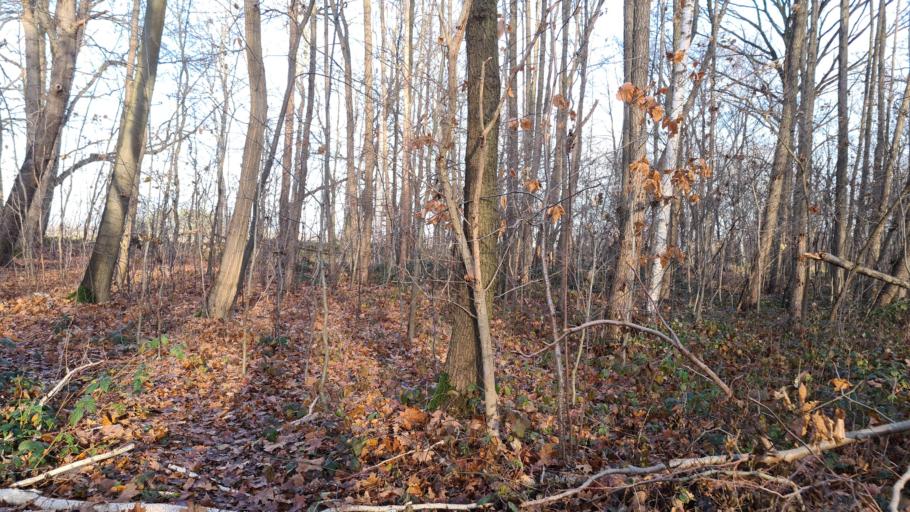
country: DE
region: Brandenburg
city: Doberlug-Kirchhain
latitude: 51.6318
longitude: 13.5809
